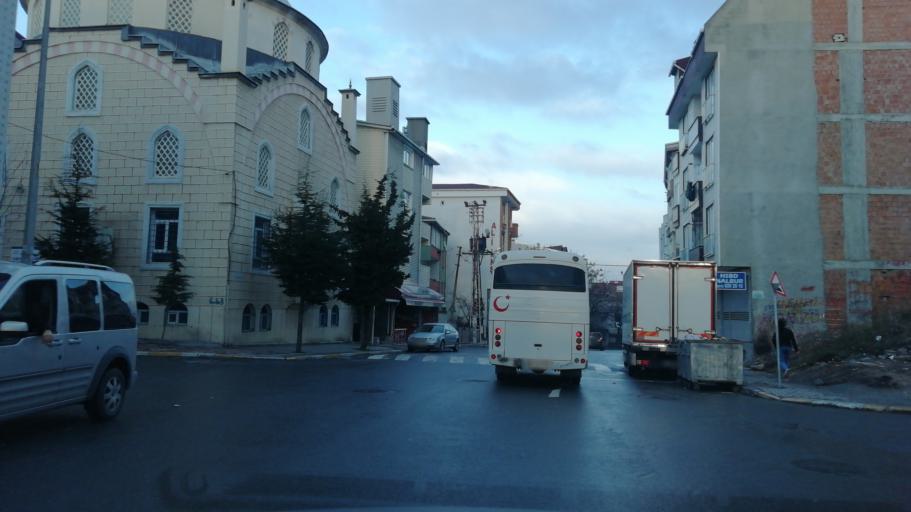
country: TR
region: Istanbul
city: Esenyurt
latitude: 41.0292
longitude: 28.6951
